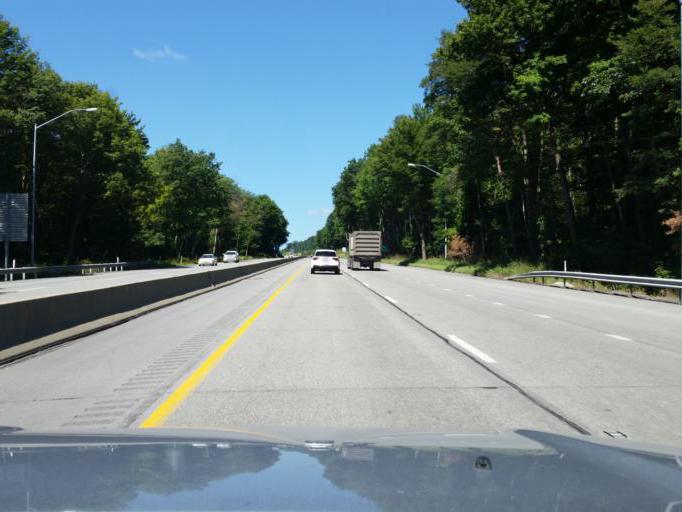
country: US
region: Pennsylvania
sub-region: Cambria County
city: Mundys Corner
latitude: 40.4503
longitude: -78.8428
